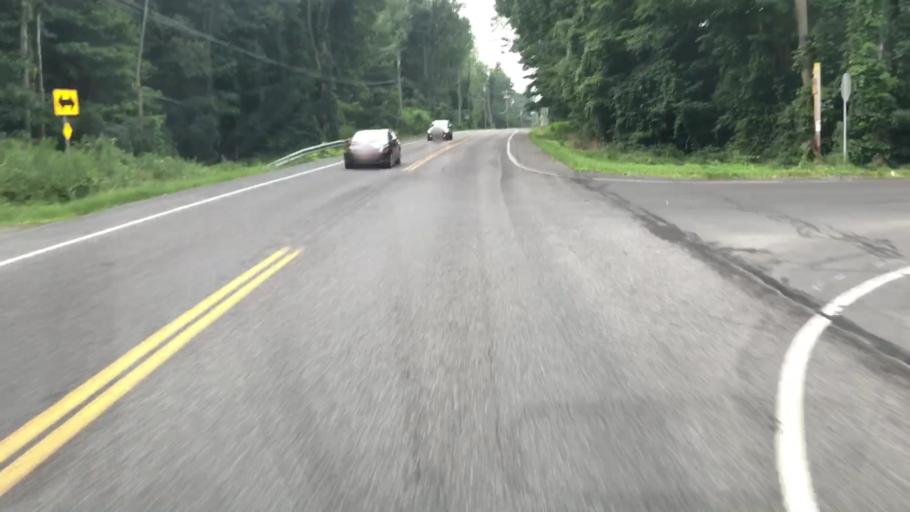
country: US
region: New York
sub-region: Onondaga County
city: Liverpool
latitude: 43.1641
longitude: -76.1947
